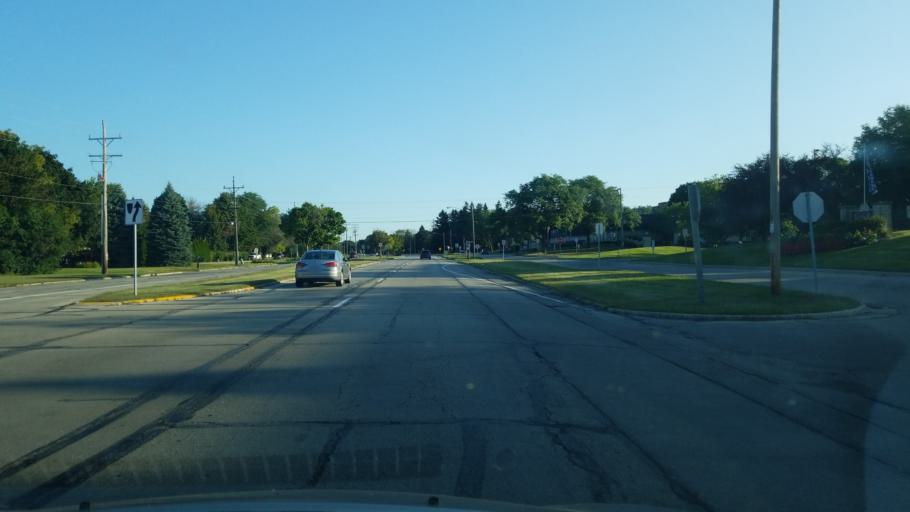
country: US
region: Wisconsin
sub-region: Milwaukee County
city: Brown Deer
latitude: 43.1885
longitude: -87.9643
